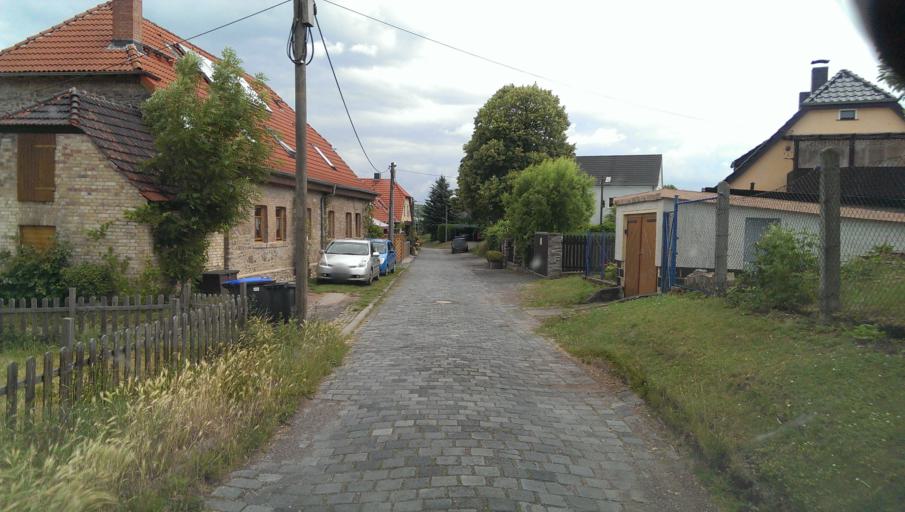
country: DE
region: Saxony-Anhalt
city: Roblingen am See
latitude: 51.4901
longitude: 11.7024
